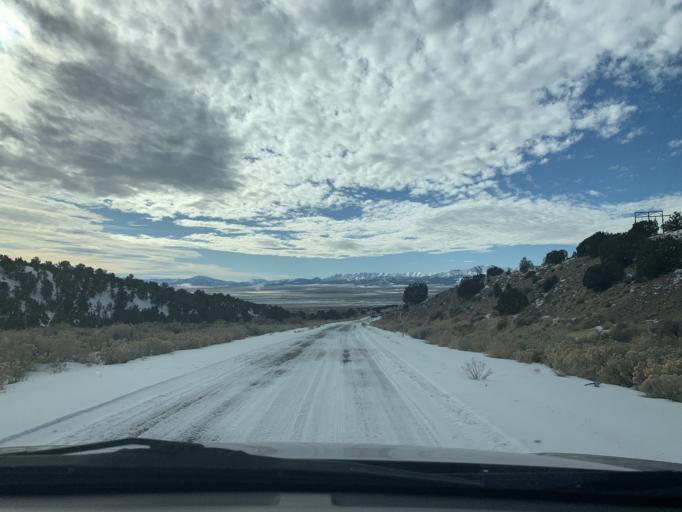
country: US
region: Utah
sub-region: Tooele County
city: Tooele
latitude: 40.3080
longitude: -112.2545
